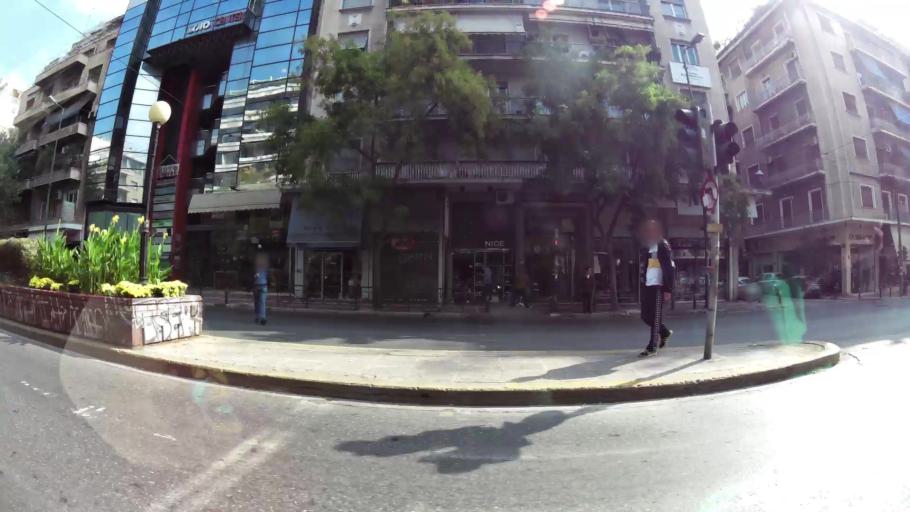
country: GR
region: Attica
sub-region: Nomarchia Athinas
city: Kipseli
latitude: 37.9981
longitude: 23.7329
